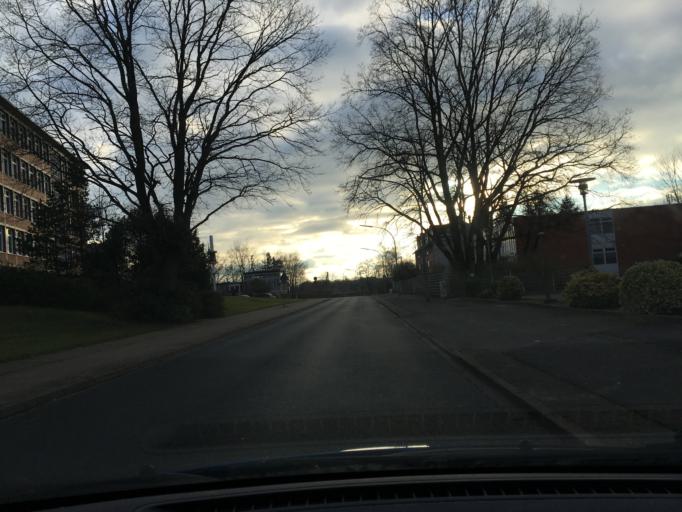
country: DE
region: Lower Saxony
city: Lueneburg
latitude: 53.2460
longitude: 10.4224
